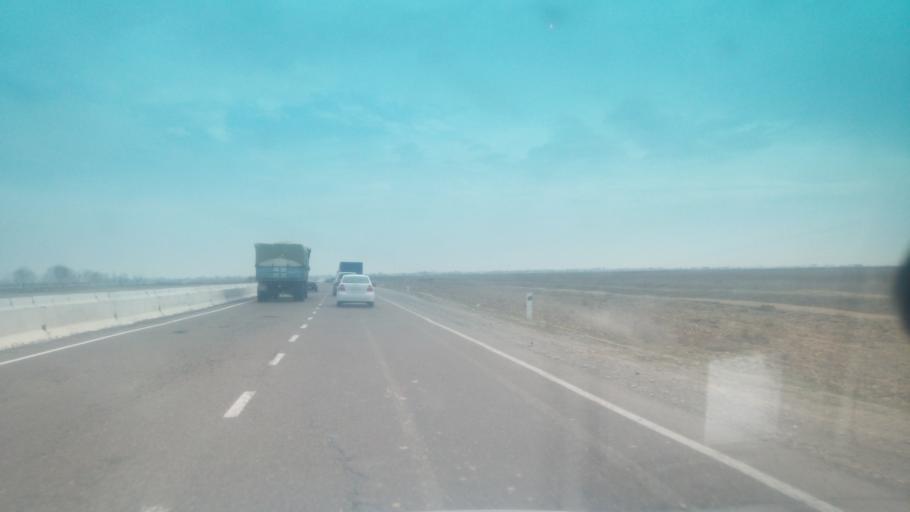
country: KZ
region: Ongtustik Qazaqstan
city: Myrzakent
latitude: 40.5134
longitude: 68.4890
